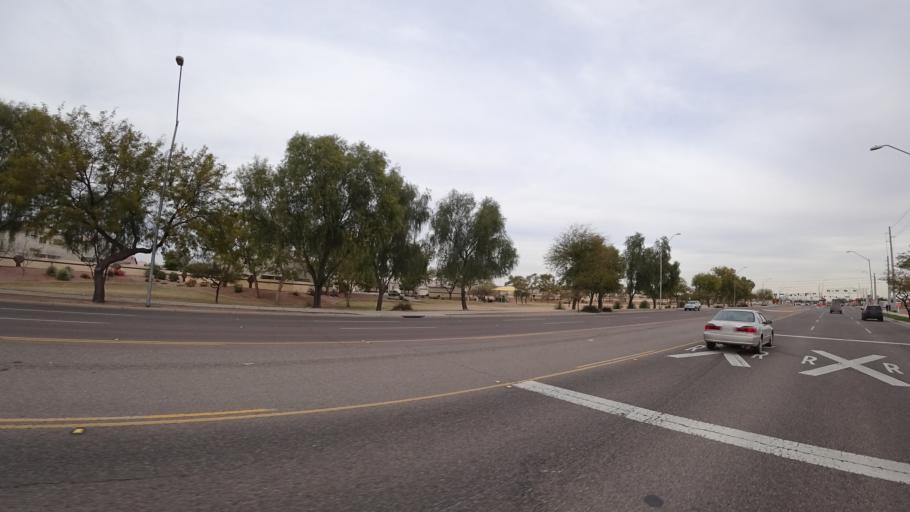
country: US
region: Arizona
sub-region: Maricopa County
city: El Mirage
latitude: 33.6090
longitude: -112.3453
